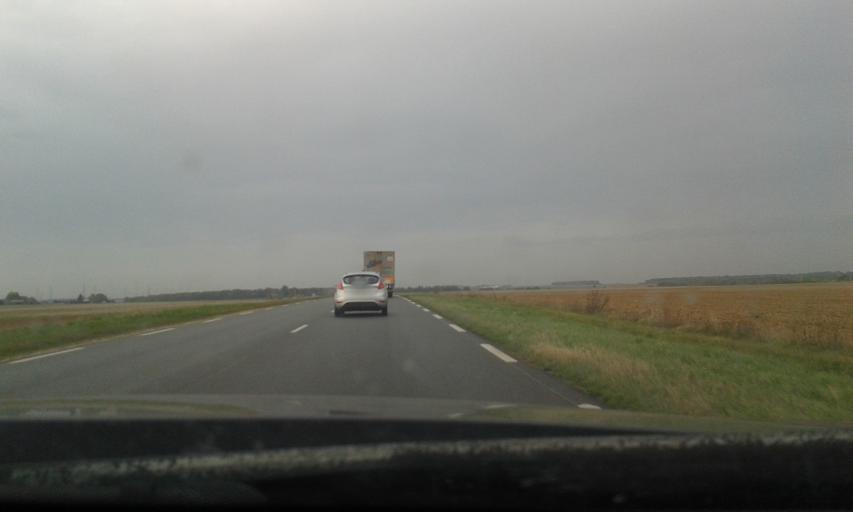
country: FR
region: Centre
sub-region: Departement d'Eure-et-Loir
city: Janville
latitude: 48.2177
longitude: 1.8082
